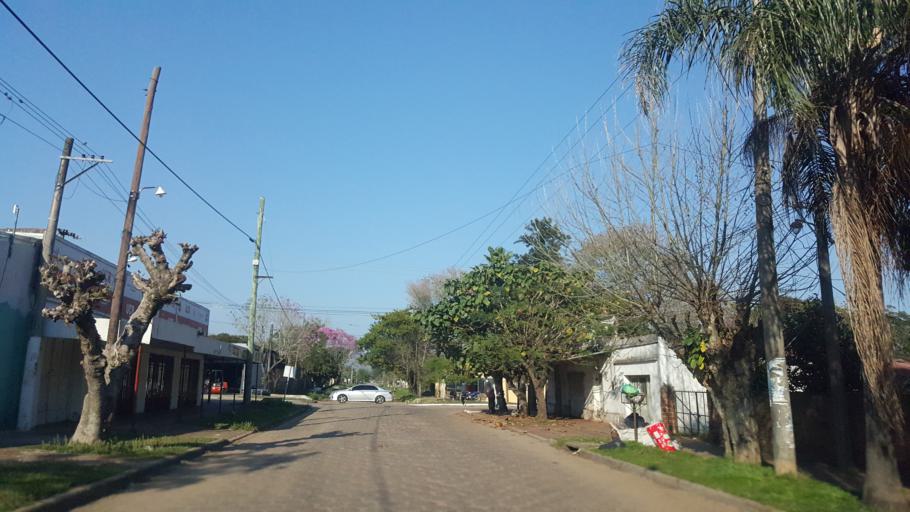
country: AR
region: Corrientes
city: Ituzaingo
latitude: -27.5901
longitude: -56.6934
